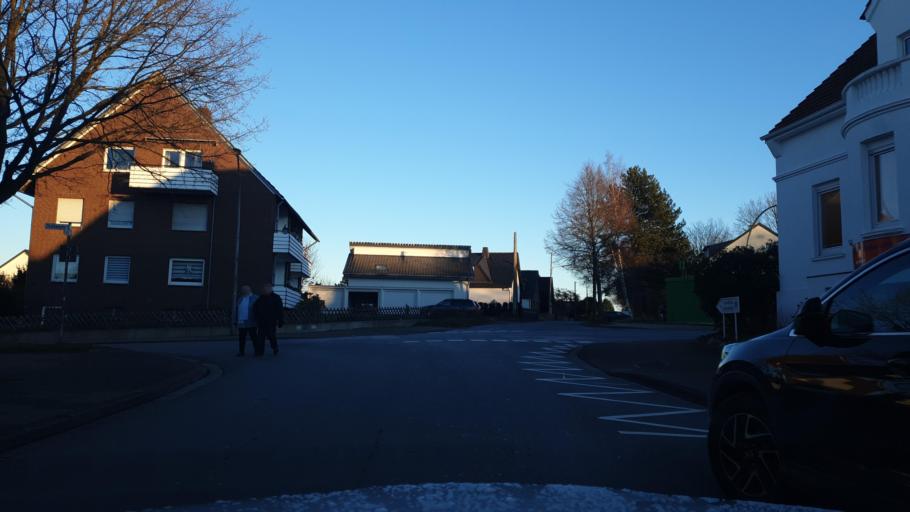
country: DE
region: North Rhine-Westphalia
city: Bad Oeynhausen
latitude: 52.1953
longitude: 8.8160
